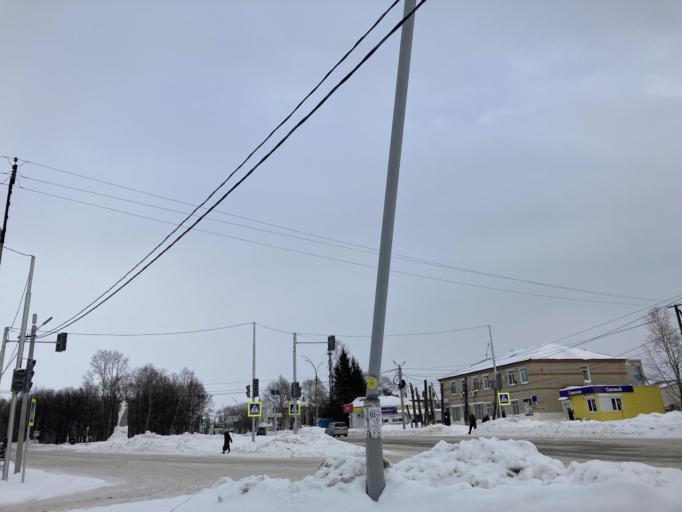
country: RU
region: Khabarovsk Krai
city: Khor
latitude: 47.9655
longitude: 135.0530
